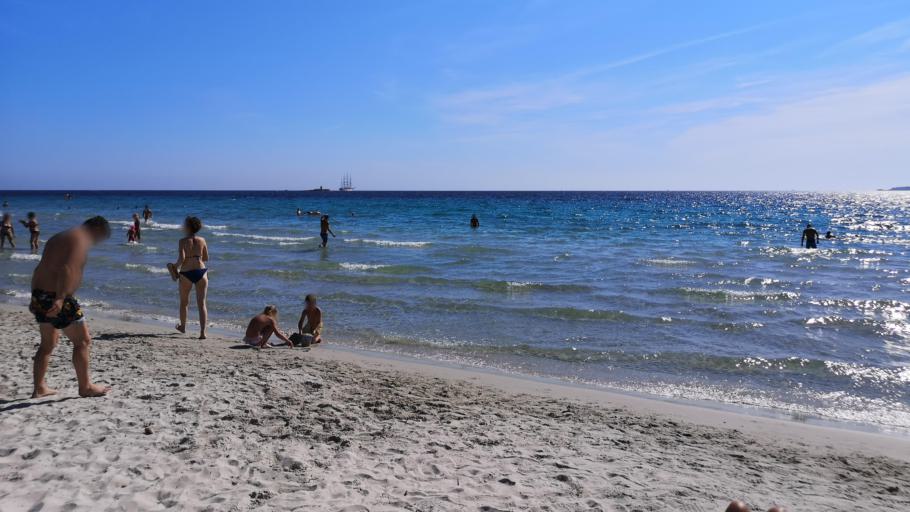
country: IT
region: Sardinia
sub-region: Provincia di Sassari
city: Alghero
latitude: 40.5824
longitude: 8.3091
